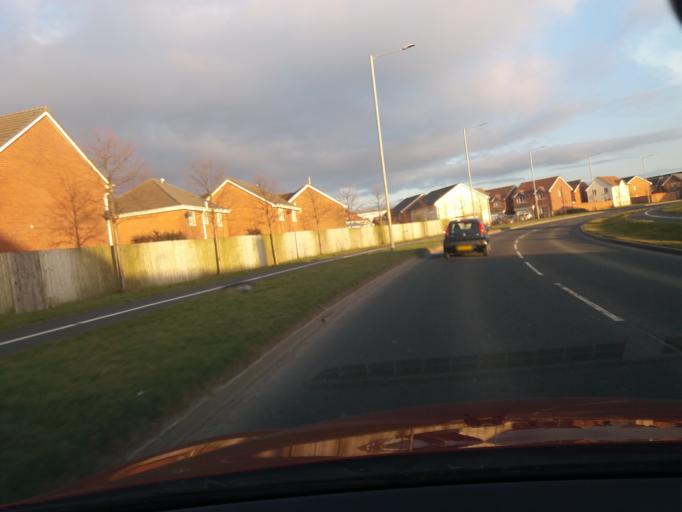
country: GB
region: England
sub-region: Lancashire
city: Euxton
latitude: 53.6769
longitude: -2.6548
